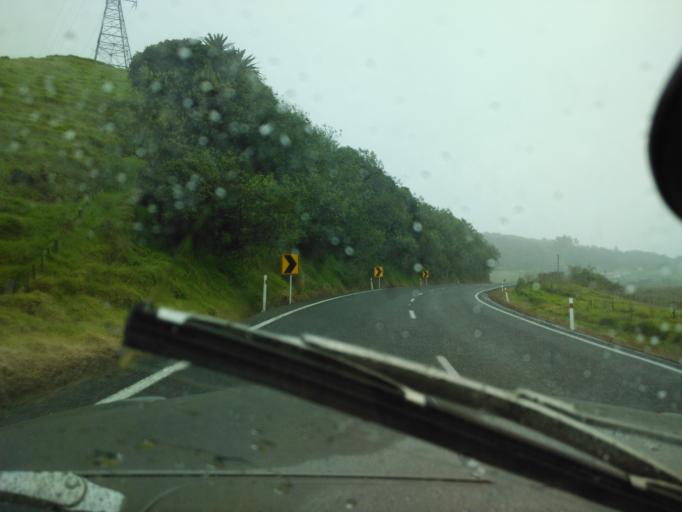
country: NZ
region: Auckland
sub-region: Auckland
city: Wellsford
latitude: -36.4309
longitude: 174.4401
